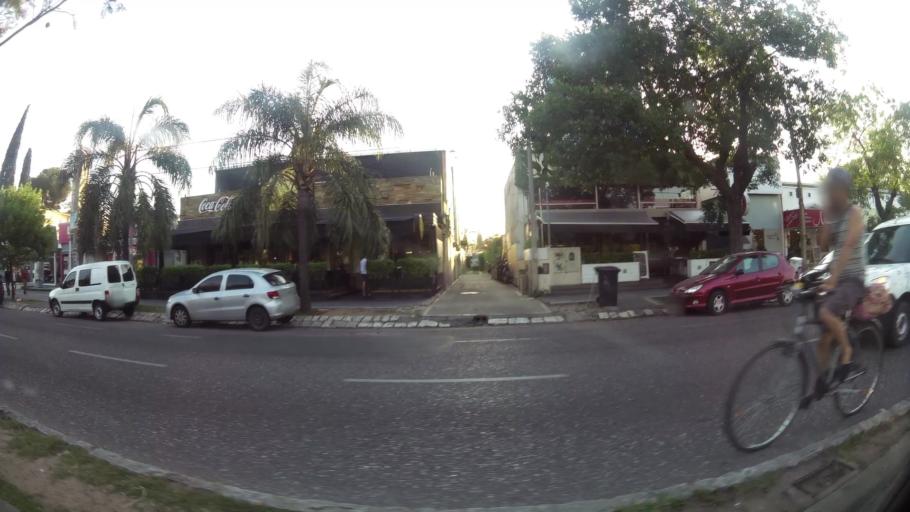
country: AR
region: Cordoba
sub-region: Departamento de Capital
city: Cordoba
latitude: -31.3710
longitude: -64.2310
